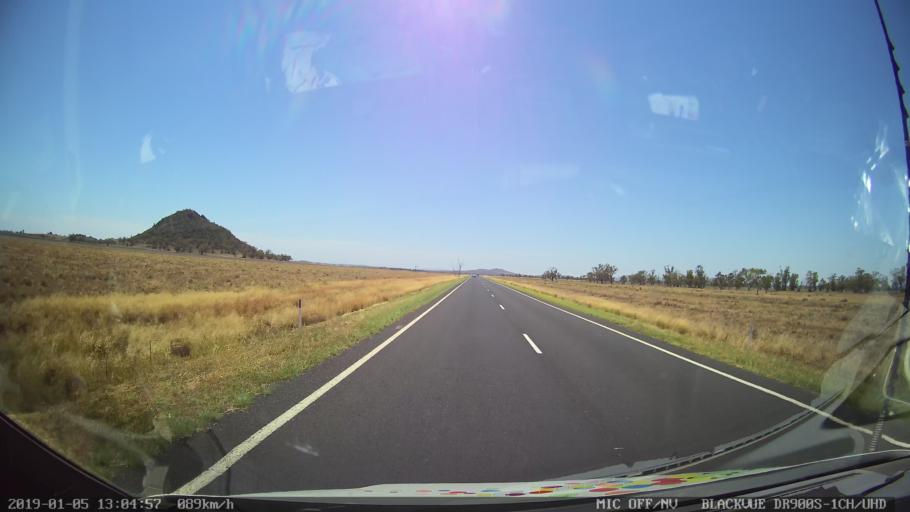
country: AU
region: New South Wales
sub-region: Gunnedah
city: Gunnedah
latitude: -31.0992
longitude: 149.8467
